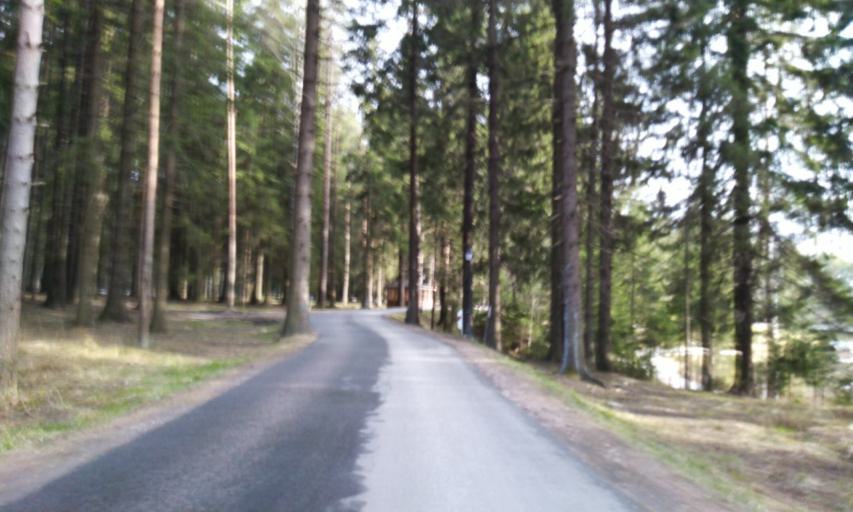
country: RU
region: Leningrad
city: Toksovo
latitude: 60.1295
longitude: 30.4526
